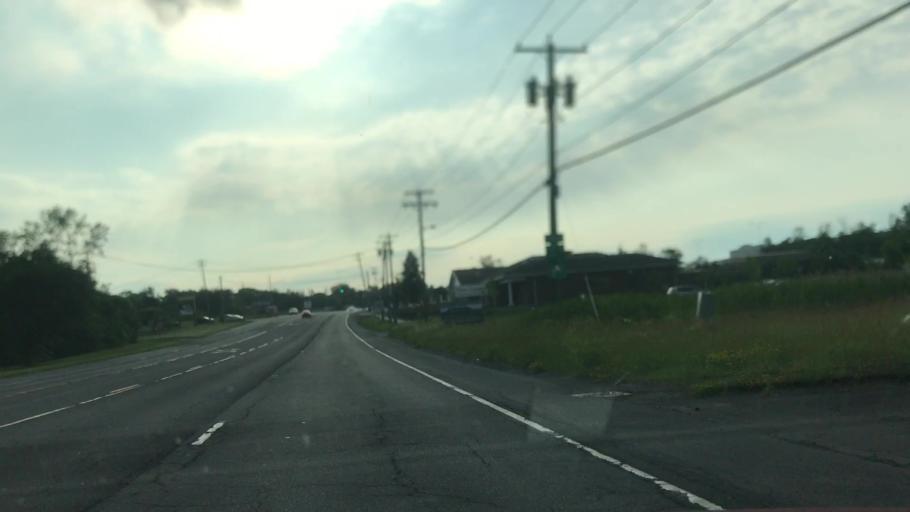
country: US
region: New York
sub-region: Albany County
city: Watervliet
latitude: 42.7380
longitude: -73.7284
